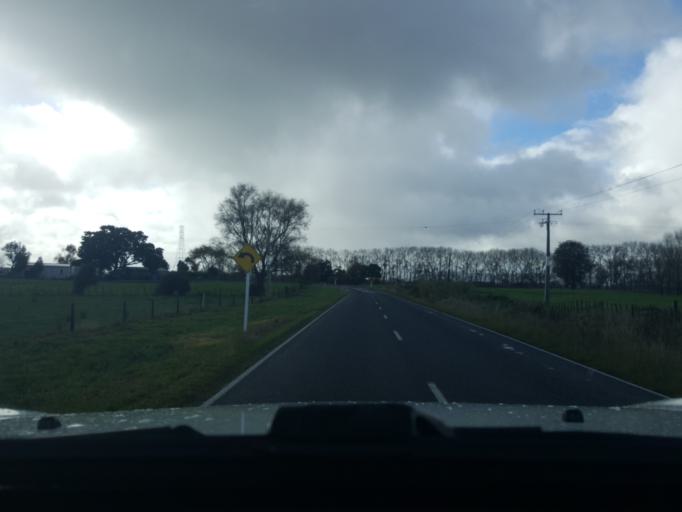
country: NZ
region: Waikato
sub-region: Waikato District
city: Te Kauwhata
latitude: -37.4431
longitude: 175.1239
